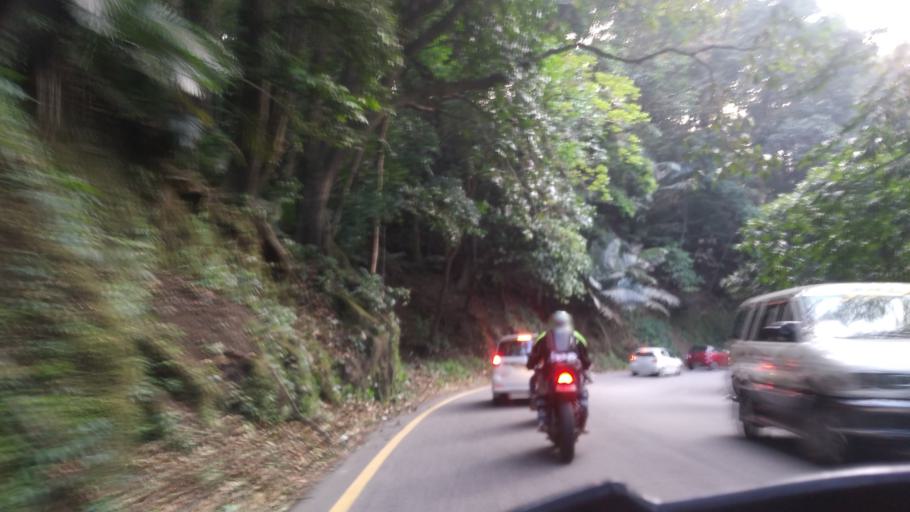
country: IN
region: Kerala
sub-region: Wayanad
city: Kalpetta
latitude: 11.5047
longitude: 76.0277
